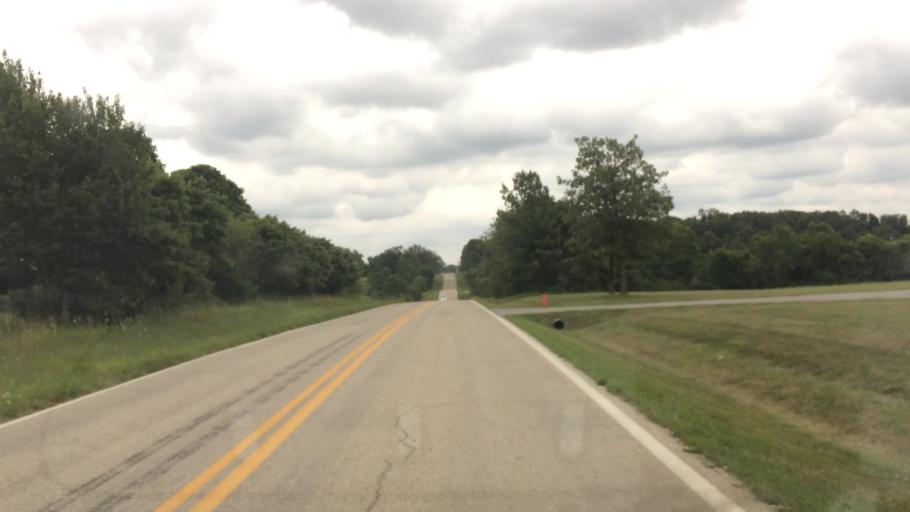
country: US
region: Missouri
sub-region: Greene County
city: Strafford
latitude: 37.3000
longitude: -93.1397
